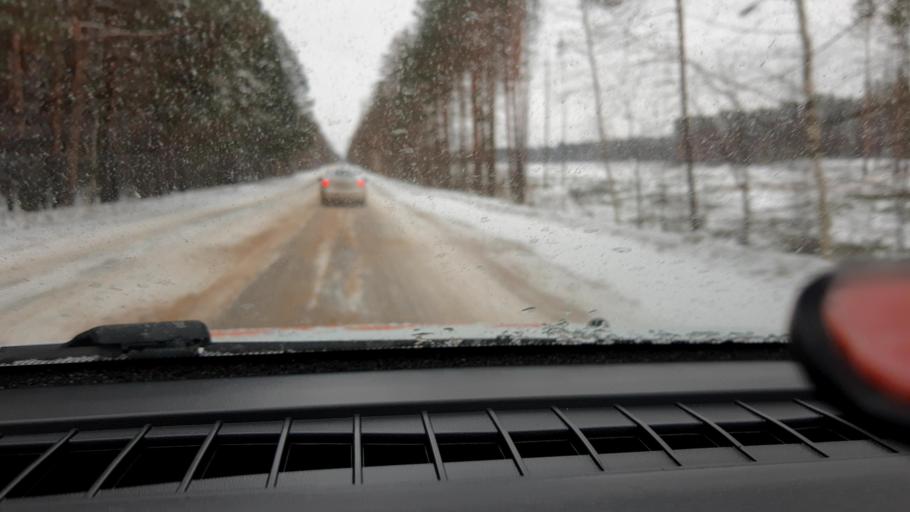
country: RU
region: Nizjnij Novgorod
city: Pamyat' Parizhskoy Kommuny
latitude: 56.2779
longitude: 44.3891
